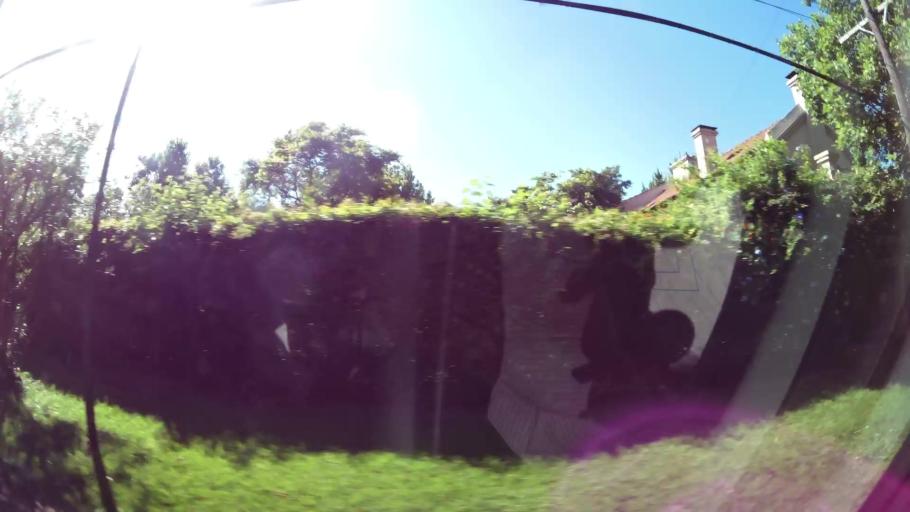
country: AR
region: Buenos Aires
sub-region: Partido de Tigre
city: Tigre
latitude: -34.4808
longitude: -58.5780
